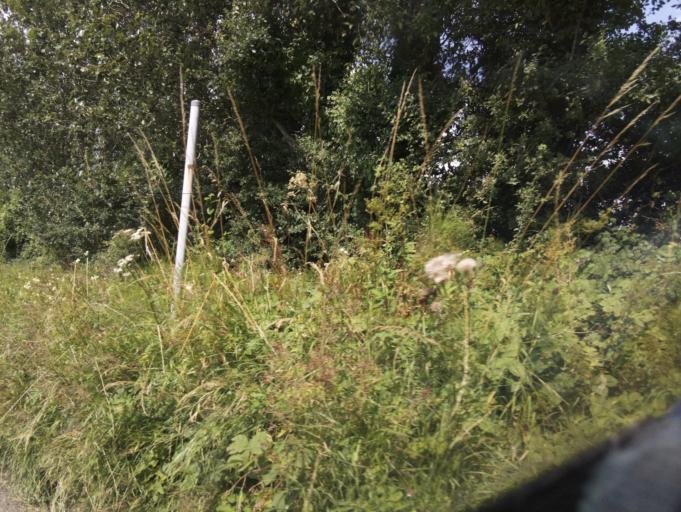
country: GB
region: England
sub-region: Wiltshire
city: Purton
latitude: 51.5879
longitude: -1.8940
